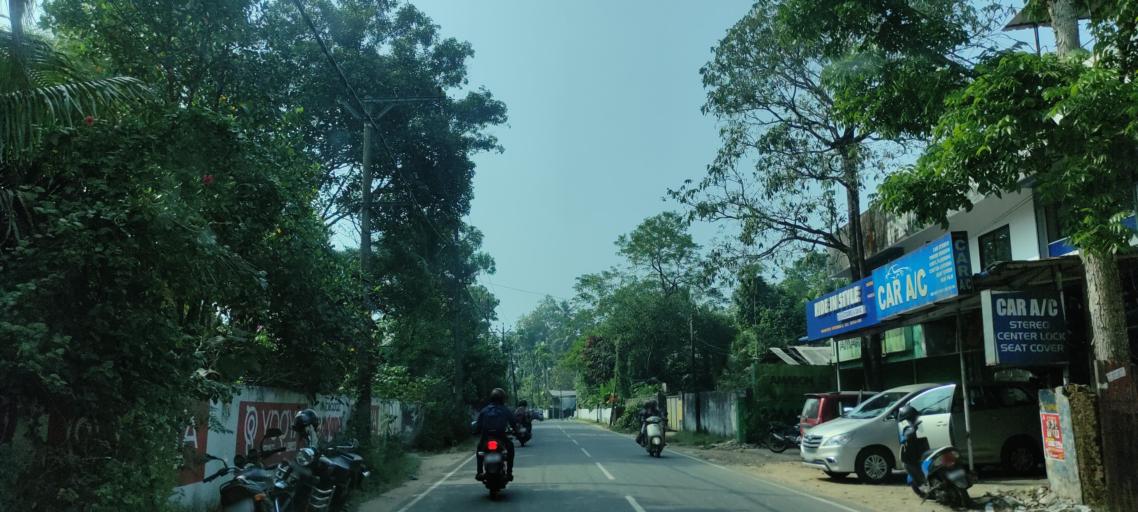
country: IN
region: Kerala
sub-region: Alappuzha
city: Vayalar
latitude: 9.6962
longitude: 76.3235
